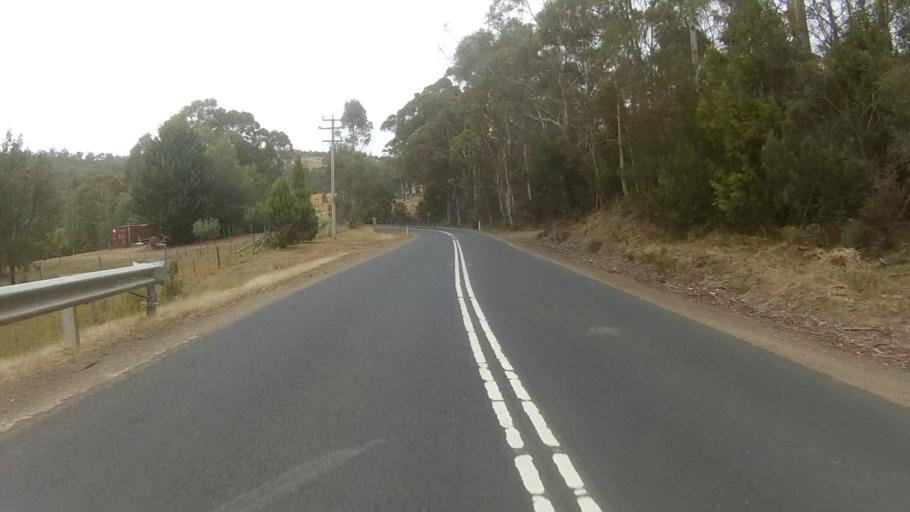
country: AU
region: Tasmania
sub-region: Kingborough
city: Margate
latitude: -43.0120
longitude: 147.2433
